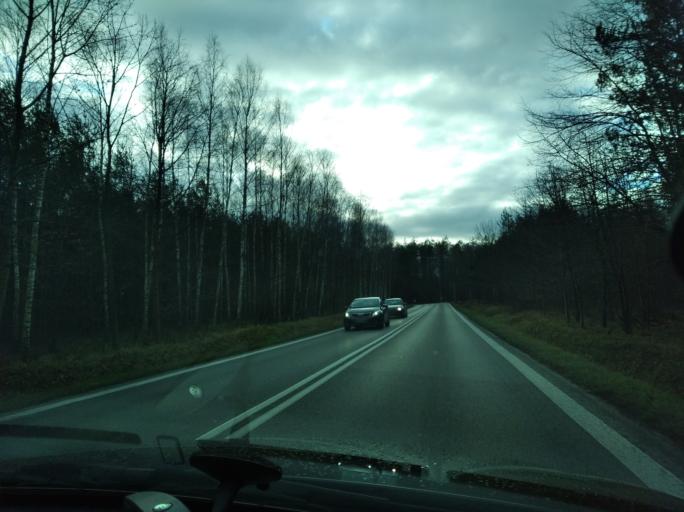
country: PL
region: Subcarpathian Voivodeship
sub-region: Powiat lancucki
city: Rakszawa
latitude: 50.1340
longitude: 22.2353
